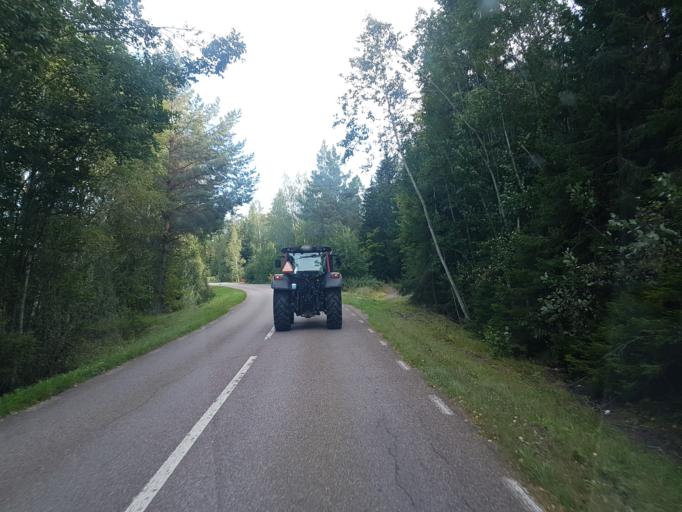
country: SE
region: Dalarna
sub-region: Saters Kommun
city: Saeter
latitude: 60.3660
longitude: 15.7174
